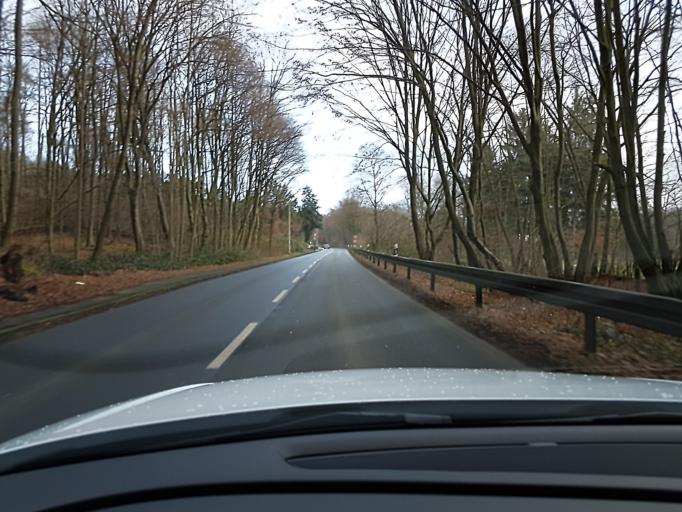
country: DE
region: North Rhine-Westphalia
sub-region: Regierungsbezirk Dusseldorf
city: Essen
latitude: 51.4016
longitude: 6.9995
